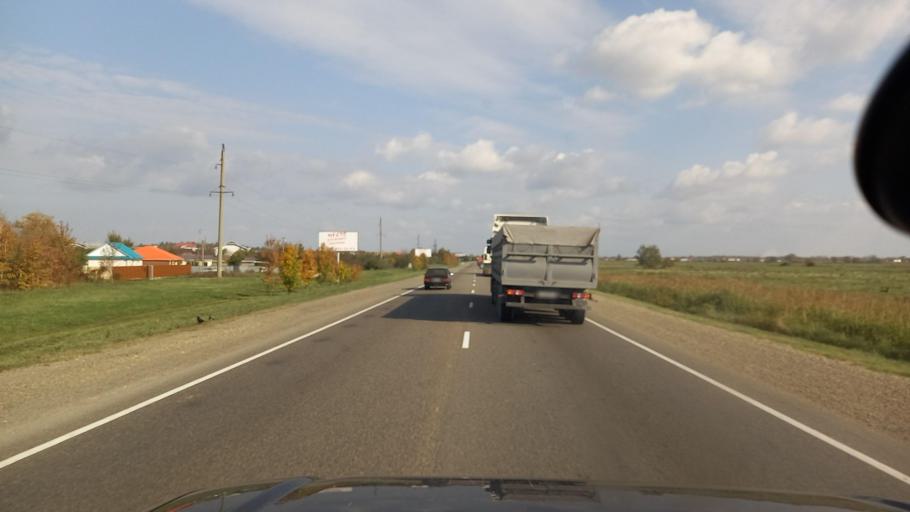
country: RU
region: Krasnodarskiy
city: Abinsk
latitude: 44.8516
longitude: 38.1846
